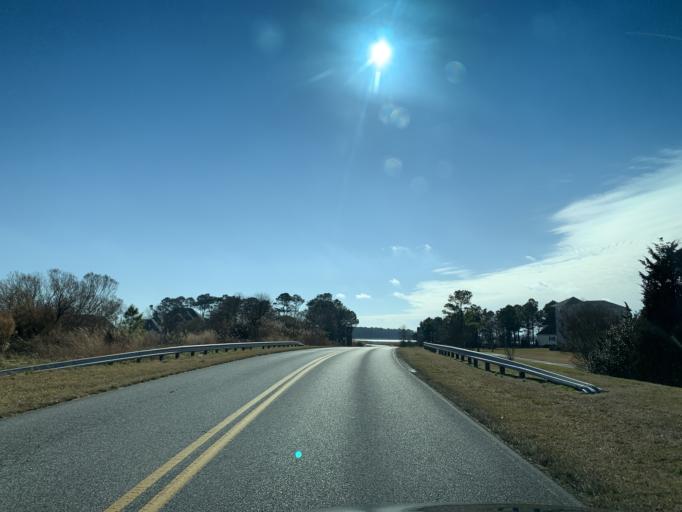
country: US
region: Maryland
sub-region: Worcester County
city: Ocean Pines
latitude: 38.4070
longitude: -75.1089
